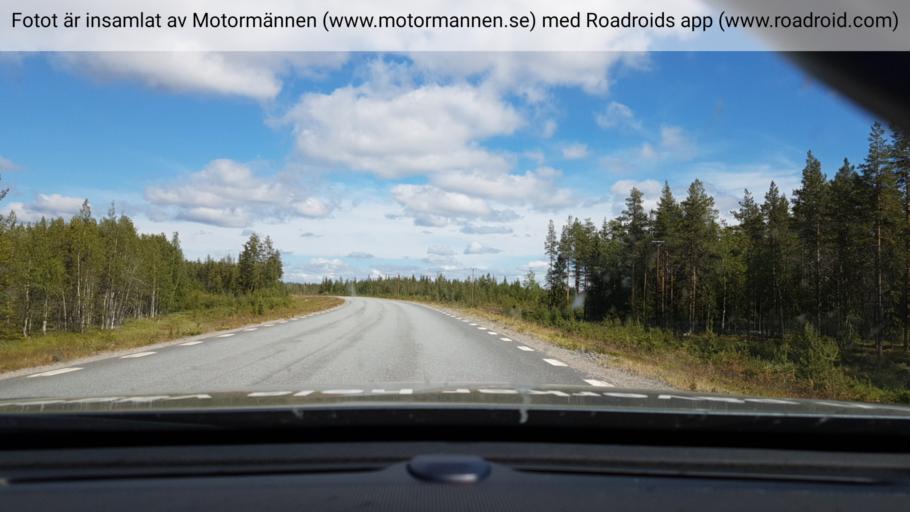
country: SE
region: Vaesterbotten
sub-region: Sorsele Kommun
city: Sorsele
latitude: 65.5571
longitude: 17.7593
